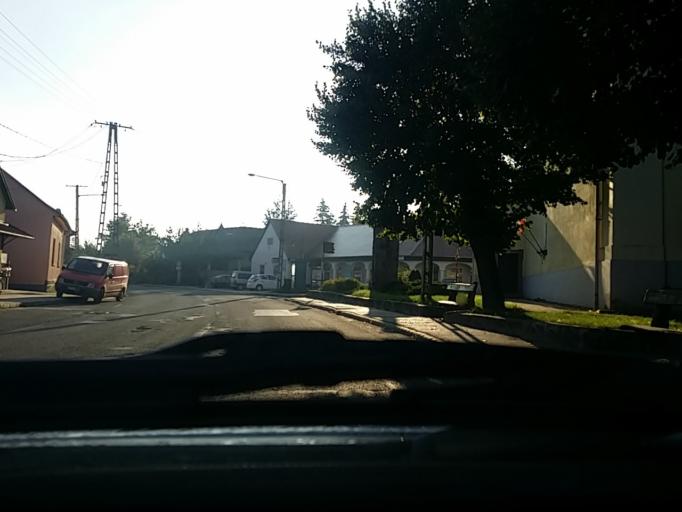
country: HU
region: Komarom-Esztergom
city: Pilismarot
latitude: 47.7636
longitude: 18.9111
